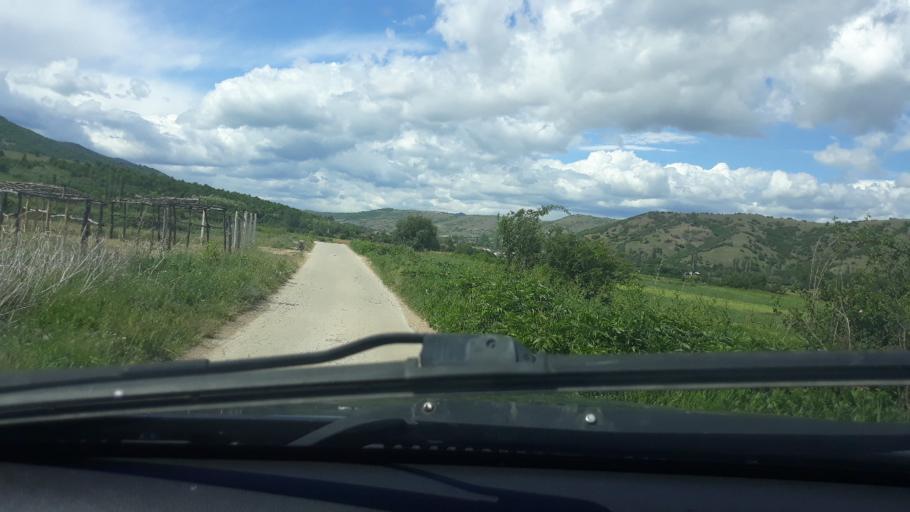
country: MK
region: Krivogastani
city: Krivogashtani
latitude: 41.3413
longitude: 21.2996
